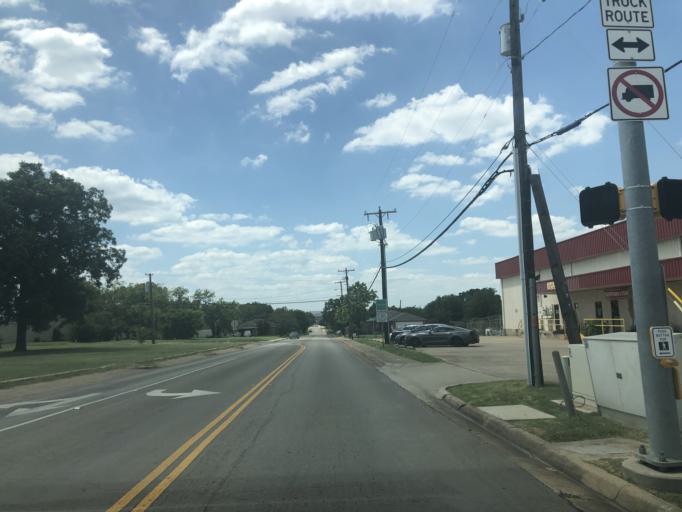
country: US
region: Texas
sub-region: Dallas County
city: Grand Prairie
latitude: 32.7398
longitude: -97.0292
